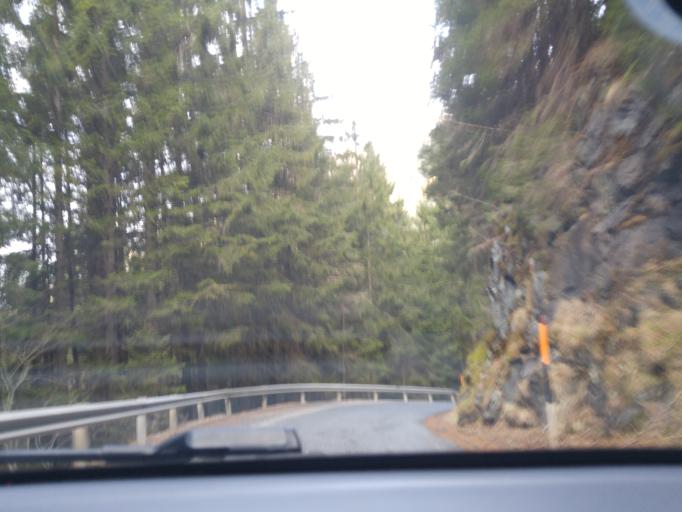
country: AT
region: Salzburg
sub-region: Politischer Bezirk Zell am See
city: Niedernsill
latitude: 47.1840
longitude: 12.6268
